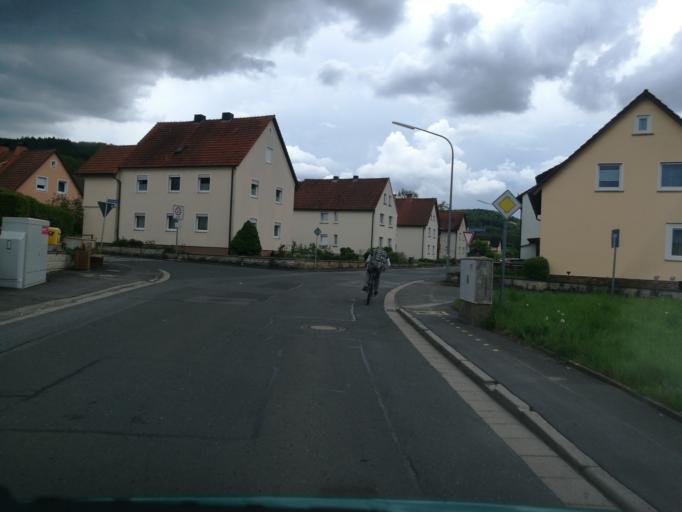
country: DE
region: Bavaria
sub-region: Upper Franconia
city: Weismain
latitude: 50.0841
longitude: 11.2475
